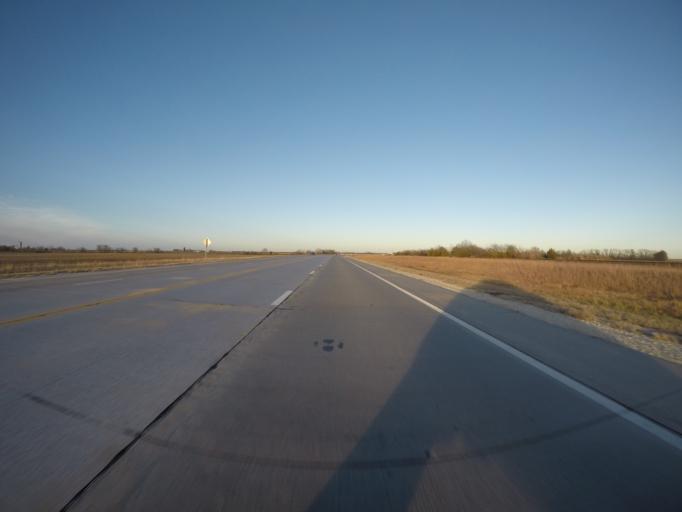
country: US
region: Kansas
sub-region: Harvey County
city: North Newton
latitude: 38.0905
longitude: -97.2866
